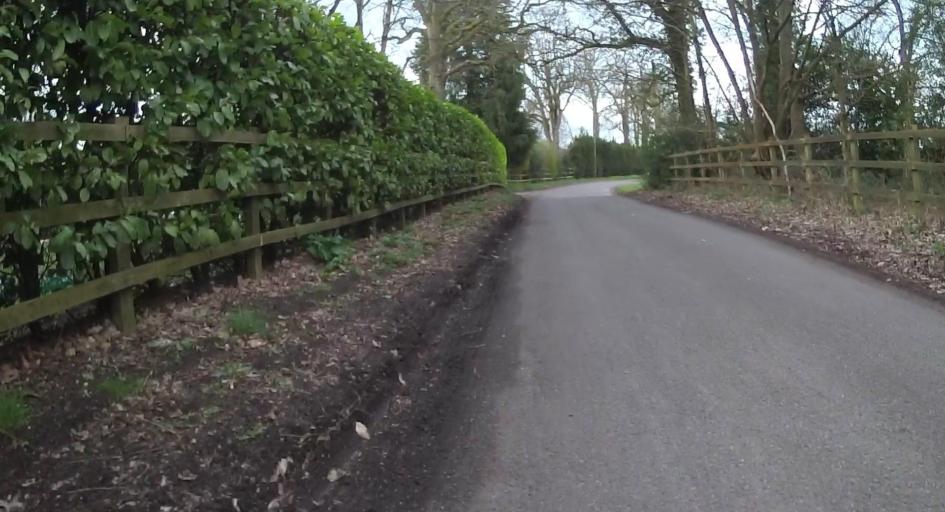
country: GB
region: England
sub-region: Surrey
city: Churt
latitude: 51.1432
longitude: -0.8047
